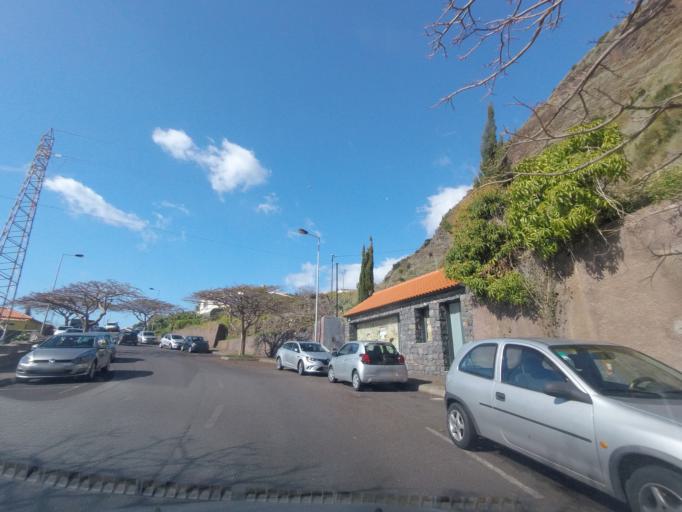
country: PT
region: Madeira
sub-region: Calheta
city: Estreito da Calheta
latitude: 32.7375
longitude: -17.2094
